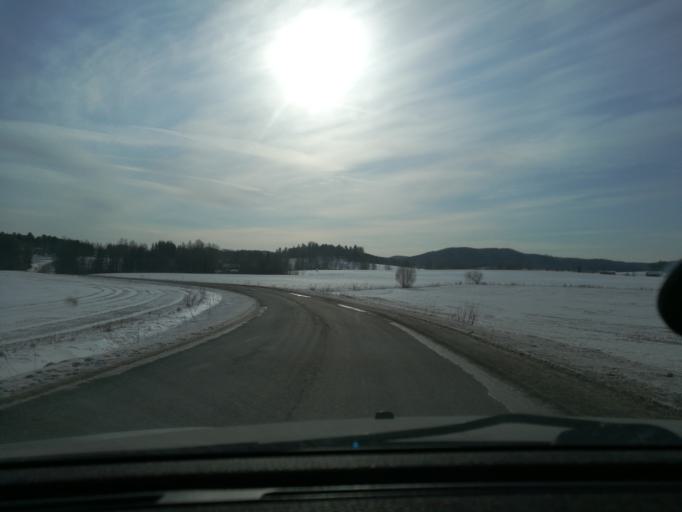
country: FI
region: Uusimaa
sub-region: Helsinki
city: Kaerkoelae
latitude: 60.5074
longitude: 23.9643
